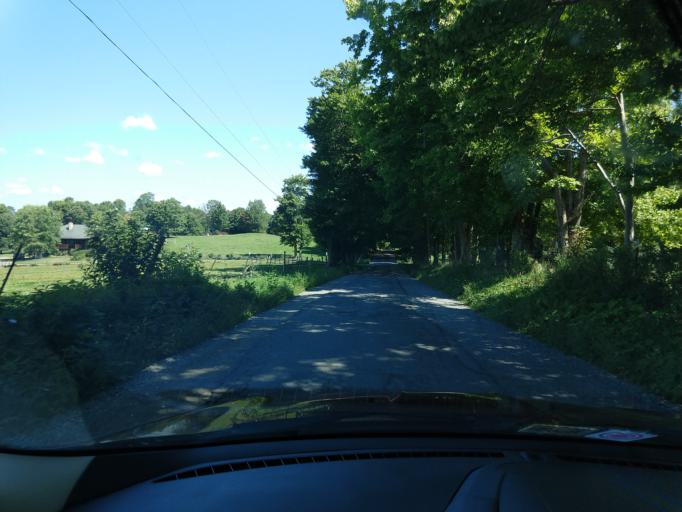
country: US
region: West Virginia
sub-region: Nicholas County
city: Craigsville
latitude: 38.2440
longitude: -80.7072
